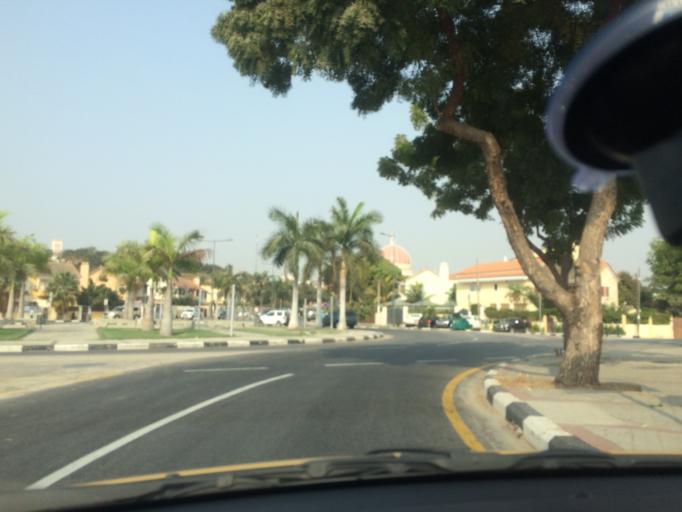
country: AO
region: Luanda
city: Luanda
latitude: -8.8202
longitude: 13.2187
